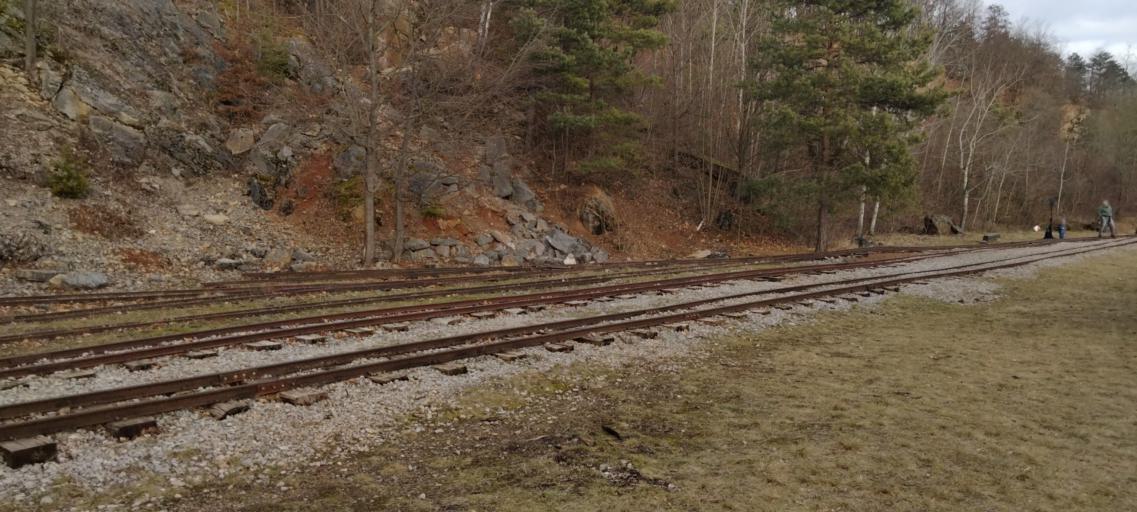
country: CZ
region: Central Bohemia
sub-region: Okres Beroun
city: Lodenice
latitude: 49.9729
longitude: 14.1429
